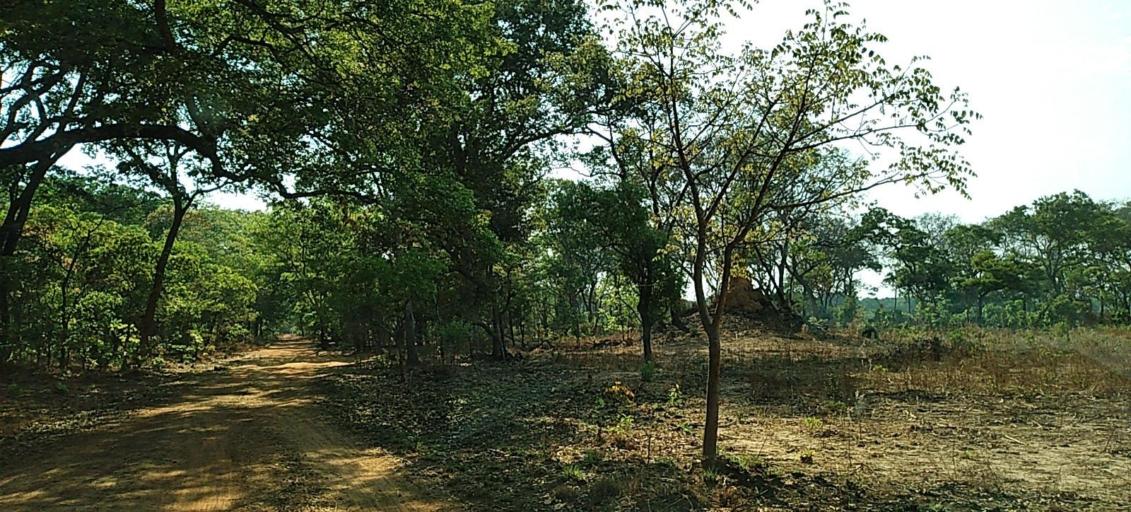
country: ZM
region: Copperbelt
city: Kalulushi
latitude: -13.0054
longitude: 27.7492
